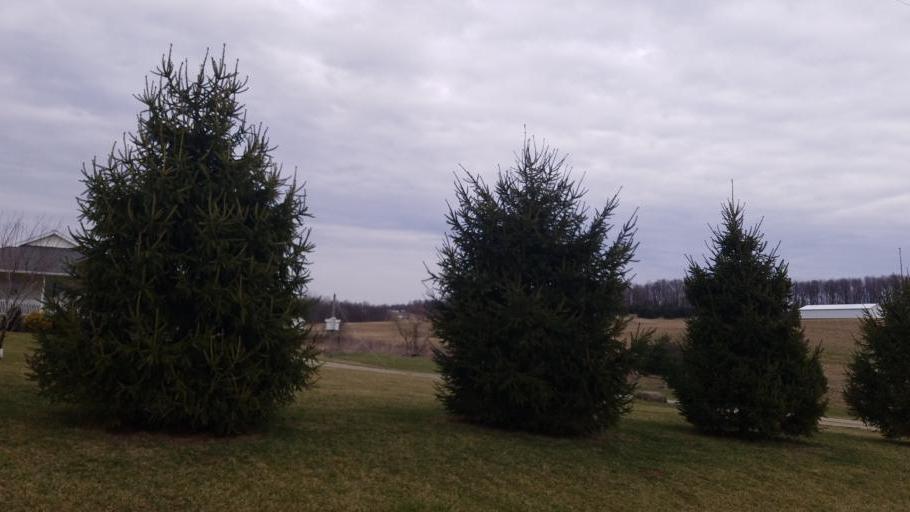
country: US
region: Ohio
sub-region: Knox County
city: Gambier
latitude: 40.5079
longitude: -82.3914
